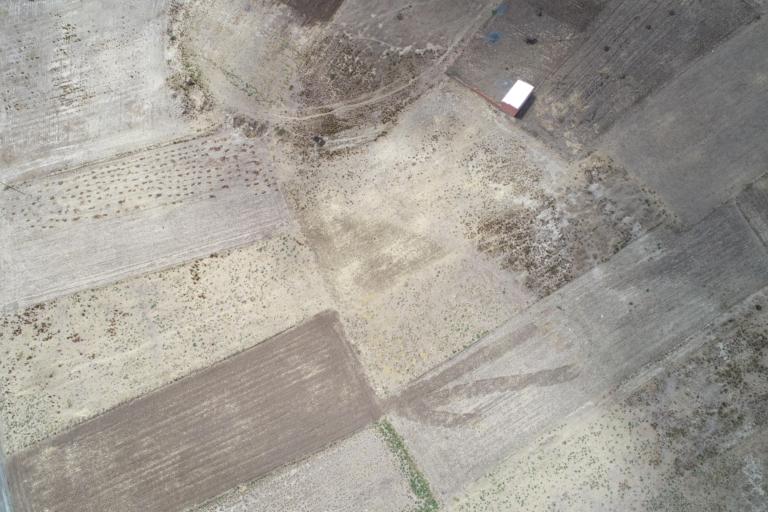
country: BO
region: La Paz
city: Achacachi
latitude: -16.0307
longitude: -68.6910
